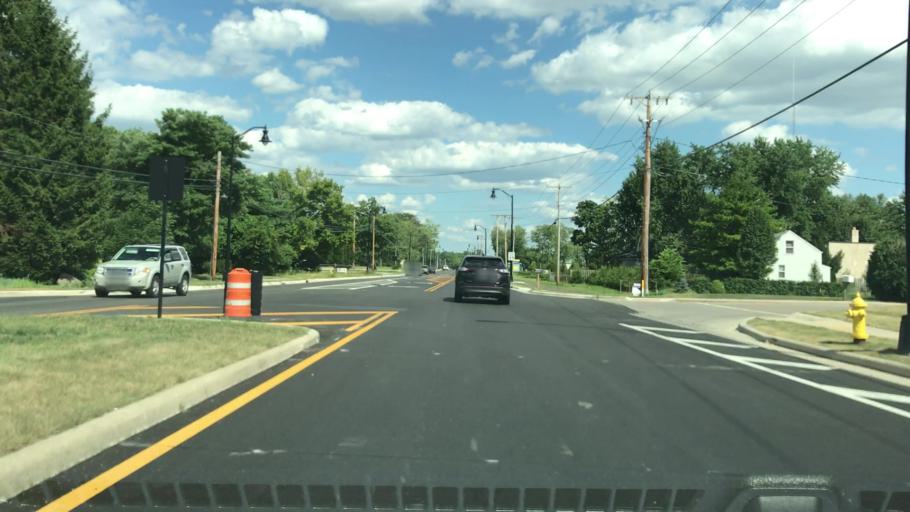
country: US
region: Ohio
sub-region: Franklin County
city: Grove City
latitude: 39.8778
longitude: -83.0361
